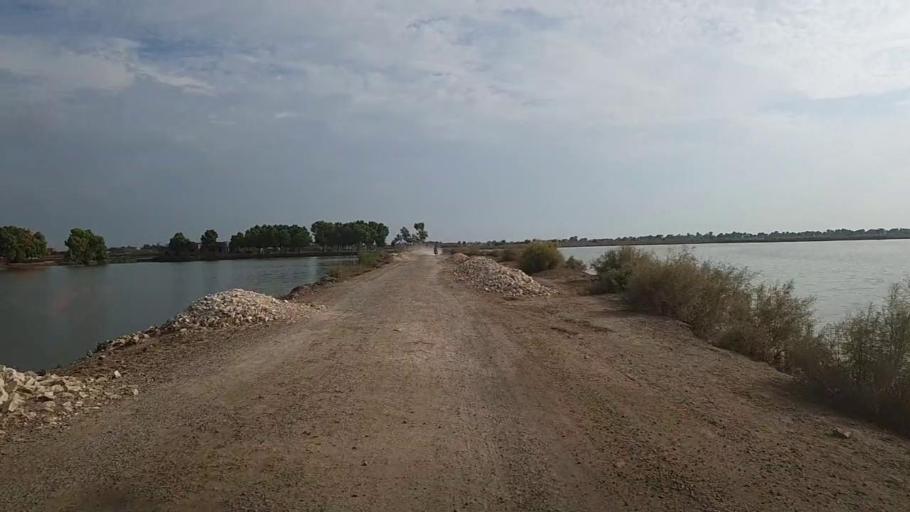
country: PK
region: Sindh
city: Thul
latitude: 28.2734
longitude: 68.8542
